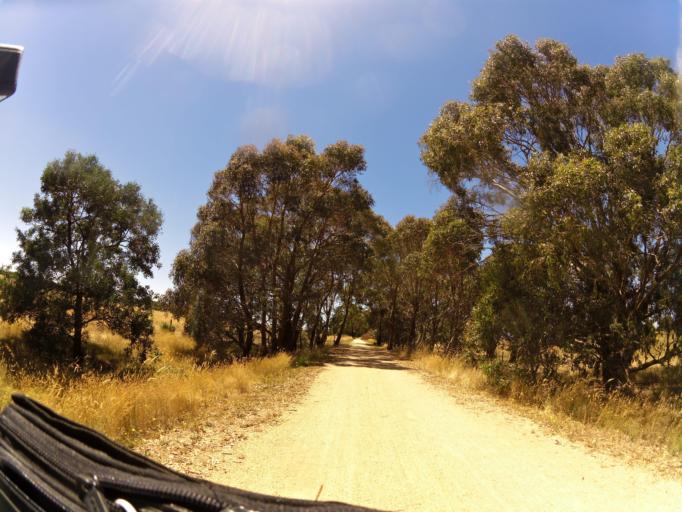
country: AU
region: Victoria
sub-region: Ballarat North
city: Delacombe
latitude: -37.5602
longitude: 143.7402
